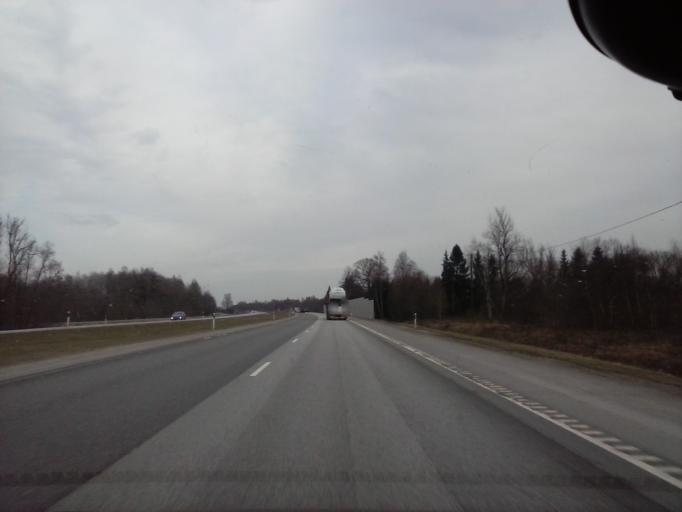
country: EE
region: Harju
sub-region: Rae vald
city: Vaida
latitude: 59.3064
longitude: 24.9420
